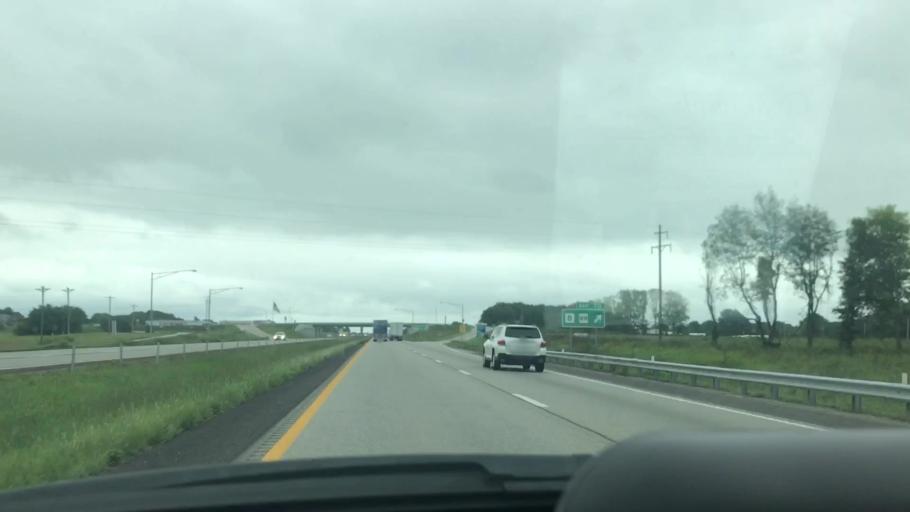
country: US
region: Missouri
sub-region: Greene County
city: Republic
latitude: 37.1995
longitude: -93.4278
